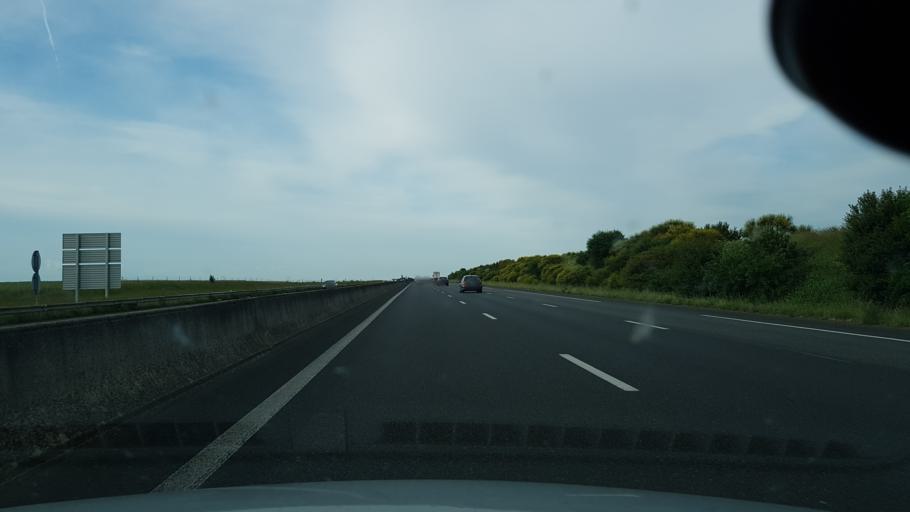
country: FR
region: Centre
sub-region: Departement du Loir-et-Cher
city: La Chaussee-Saint-Victor
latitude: 47.6342
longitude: 1.3564
